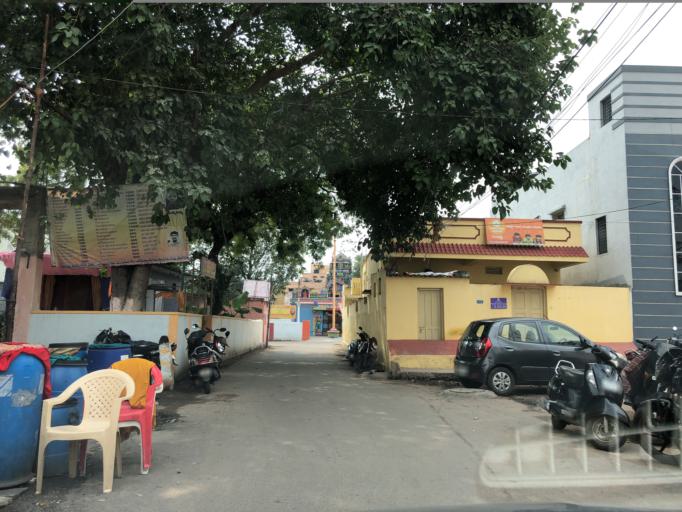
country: IN
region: Telangana
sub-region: Hyderabad
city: Malkajgiri
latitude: 17.4466
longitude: 78.4842
